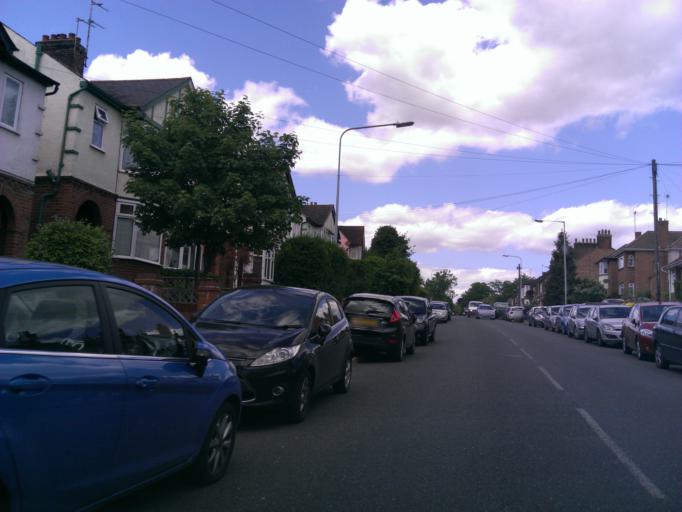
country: GB
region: England
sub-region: Essex
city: Colchester
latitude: 51.8777
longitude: 0.9188
